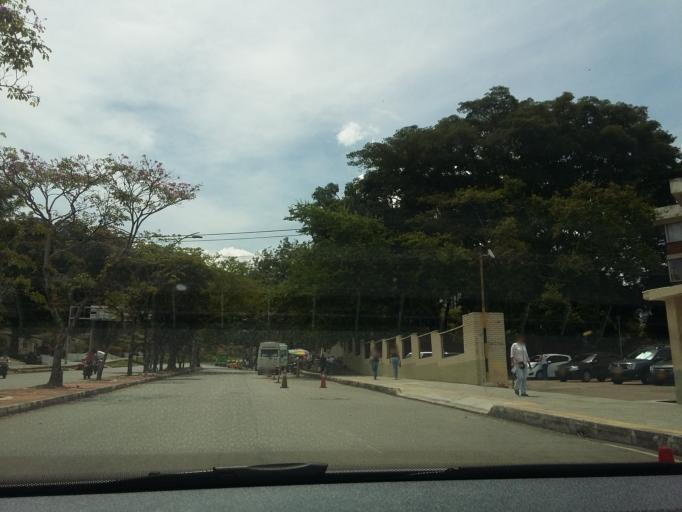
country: CO
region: Santander
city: Bucaramanga
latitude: 7.1310
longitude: -73.1111
